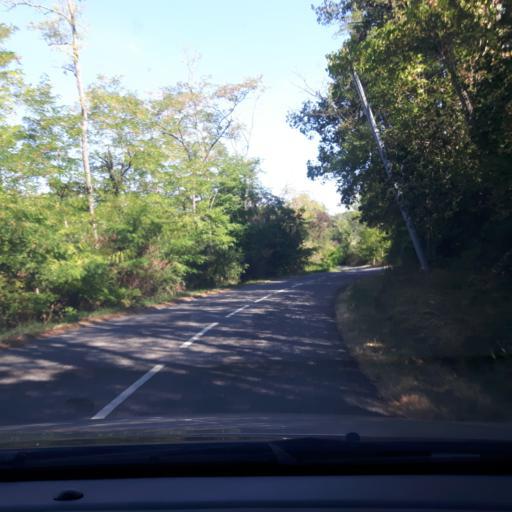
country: FR
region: Midi-Pyrenees
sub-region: Departement de la Haute-Garonne
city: Vacquiers
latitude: 43.7733
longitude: 1.4844
